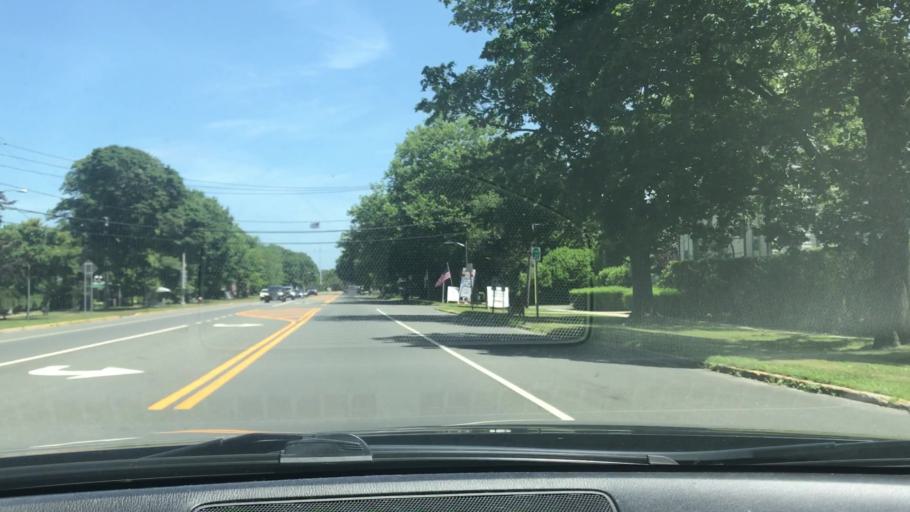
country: US
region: New York
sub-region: Suffolk County
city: Amagansett
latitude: 40.9771
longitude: -72.1379
